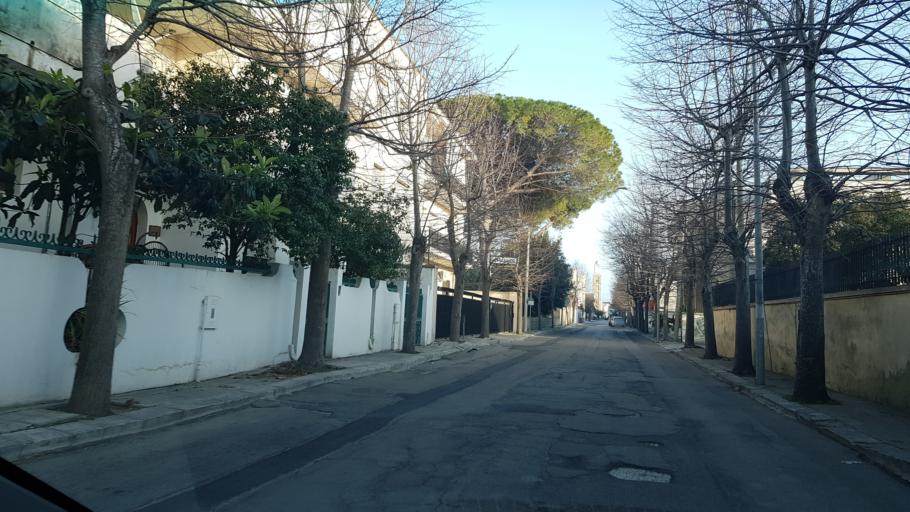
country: IT
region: Apulia
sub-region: Provincia di Lecce
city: Novoli
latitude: 40.3814
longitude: 18.0445
